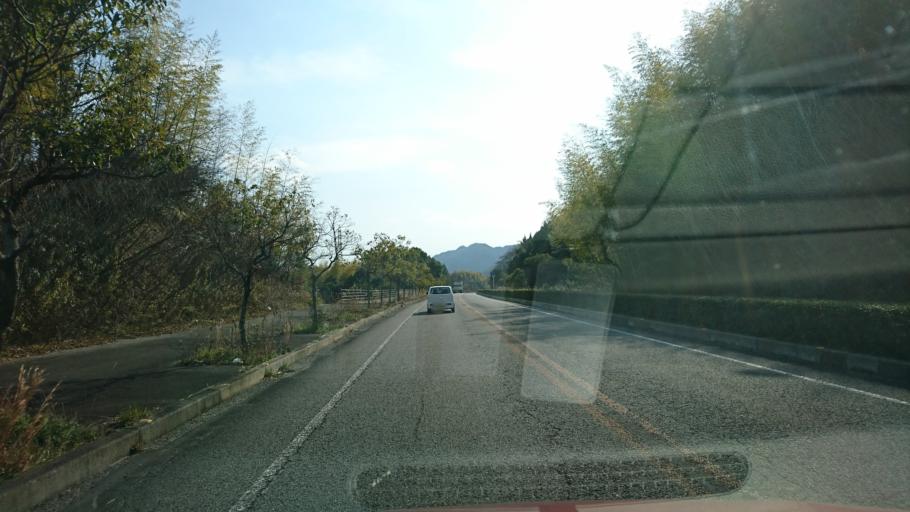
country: JP
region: Ehime
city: Saijo
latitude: 34.0131
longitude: 133.0335
